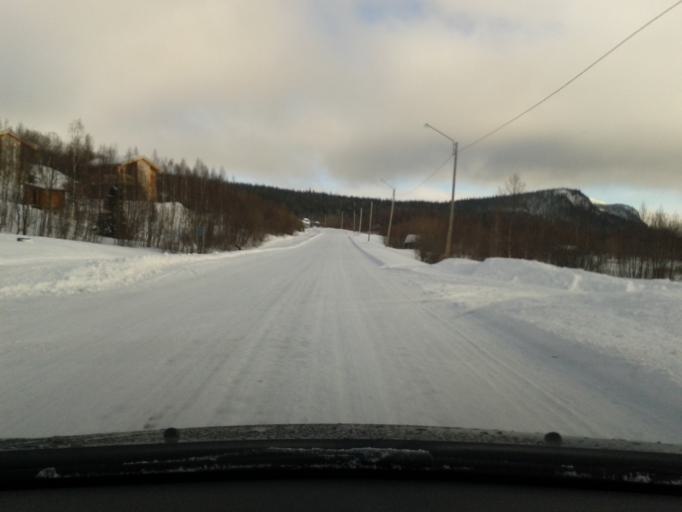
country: SE
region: Vaesterbotten
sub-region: Vilhelmina Kommun
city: Sjoberg
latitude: 65.2521
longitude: 15.5088
